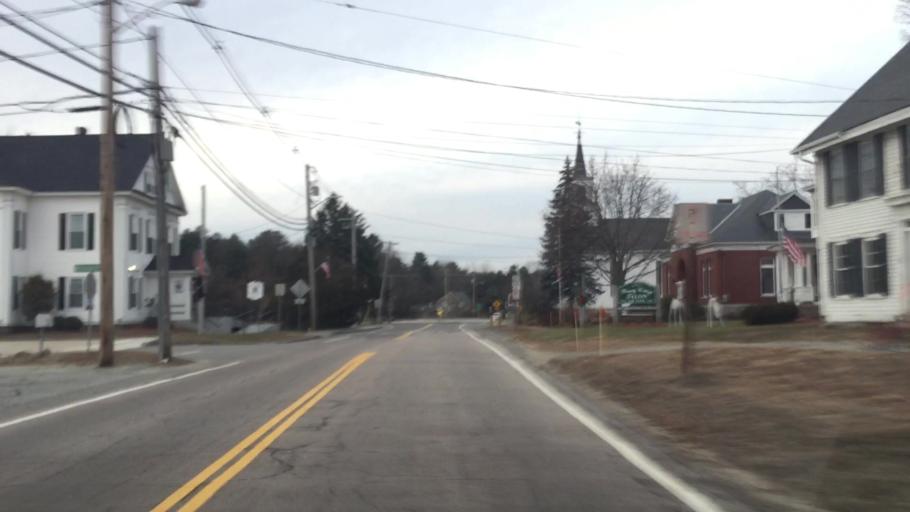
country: US
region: New Hampshire
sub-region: Hillsborough County
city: Pelham
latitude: 42.7335
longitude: -71.3213
